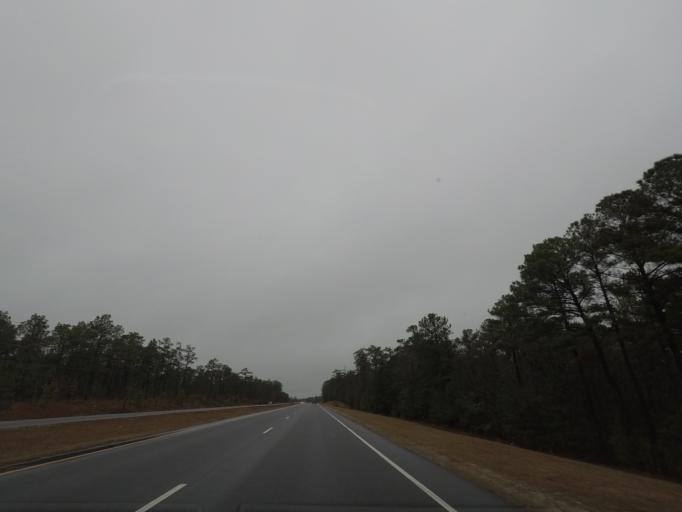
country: US
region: North Carolina
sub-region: Cumberland County
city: Spring Lake
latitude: 35.2379
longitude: -79.0205
